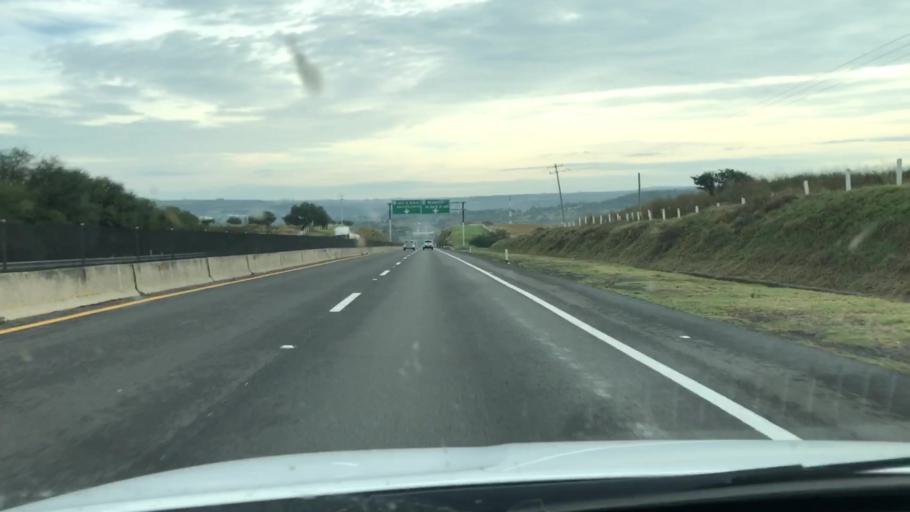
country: MX
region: Jalisco
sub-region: San Juan de los Lagos
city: Mezquitic de la Magdalena
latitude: 21.2173
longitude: -102.3204
